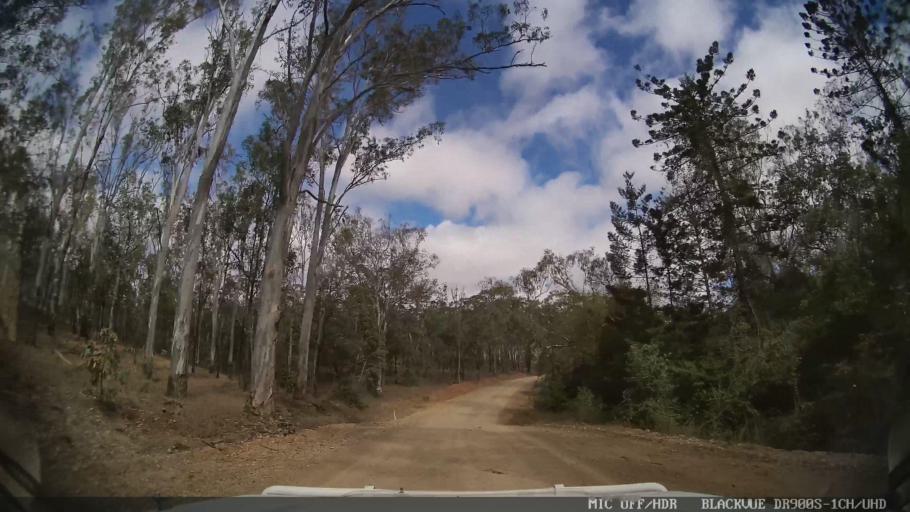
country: AU
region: Queensland
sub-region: Gladstone
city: Toolooa
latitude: -24.6844
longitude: 151.3294
